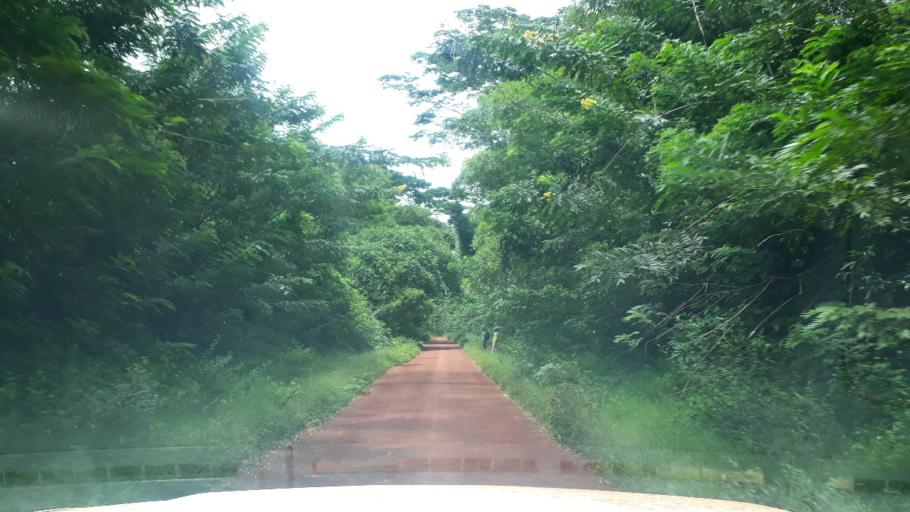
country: CD
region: Eastern Province
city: Aketi
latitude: 2.9293
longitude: 24.0885
